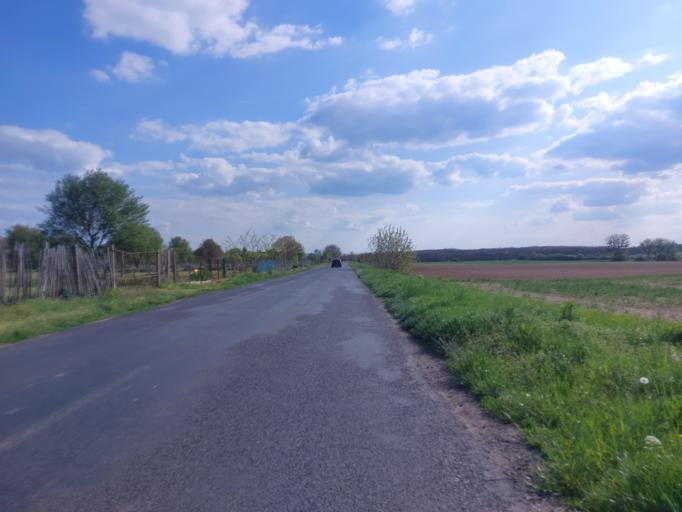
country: HU
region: Veszprem
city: Devecser
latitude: 47.1535
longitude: 17.3573
